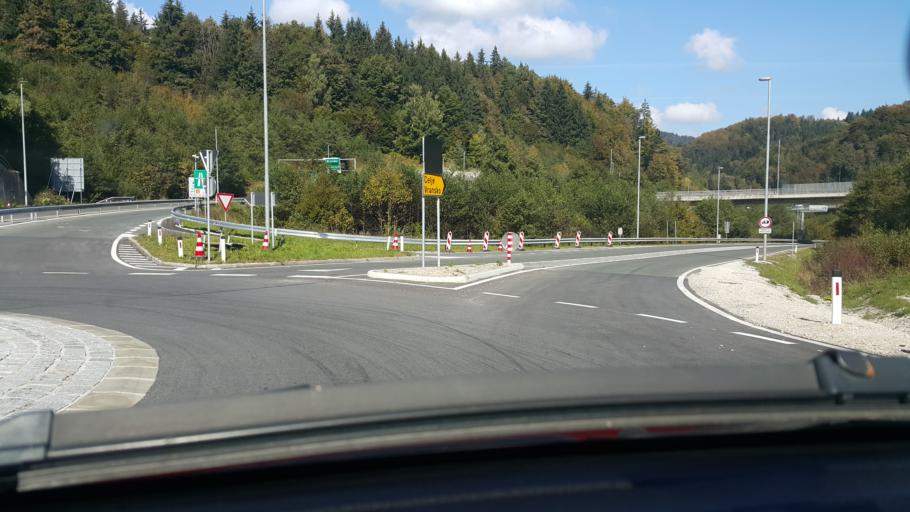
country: SI
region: Zagorje ob Savi
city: Izlake
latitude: 46.1925
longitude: 14.9003
